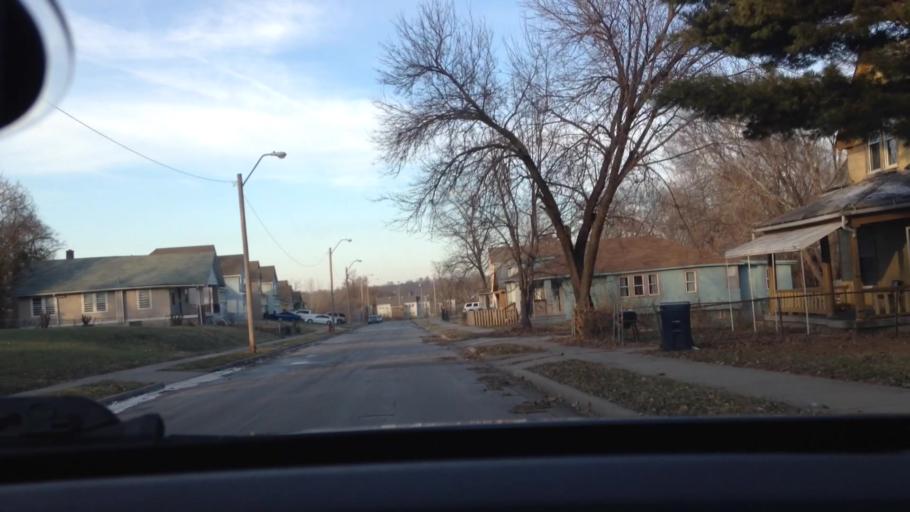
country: US
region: Missouri
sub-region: Jackson County
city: Kansas City
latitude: 39.0881
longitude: -94.5485
